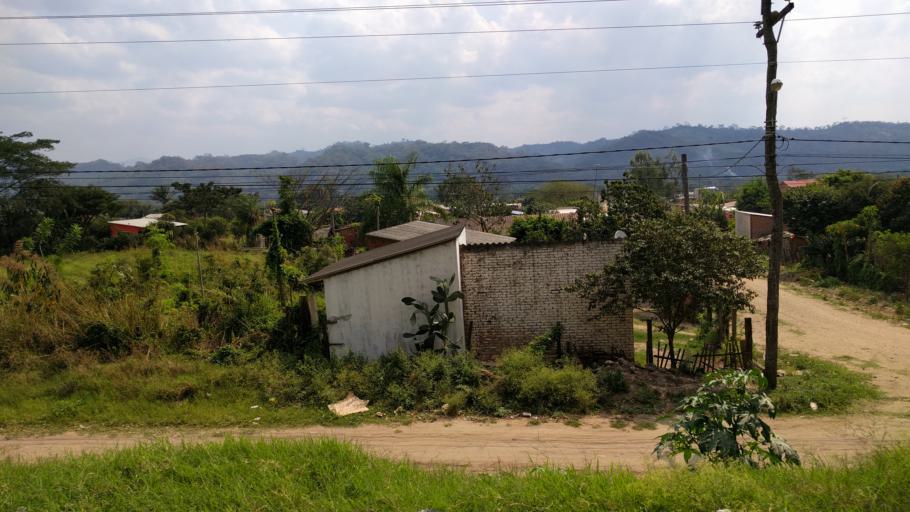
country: BO
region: Santa Cruz
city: Limoncito
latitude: -18.0226
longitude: -63.3994
